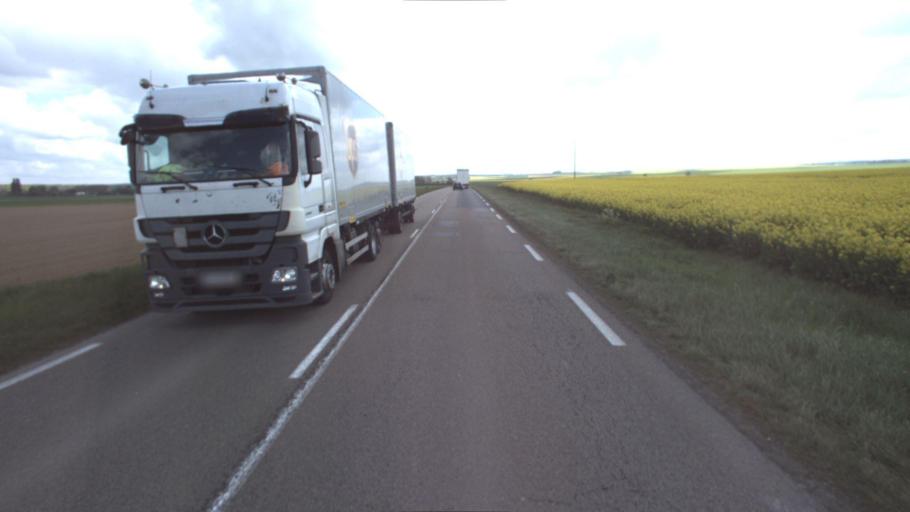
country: FR
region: Ile-de-France
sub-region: Departement de Seine-et-Marne
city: Villiers-Saint-Georges
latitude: 48.6911
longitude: 3.3485
